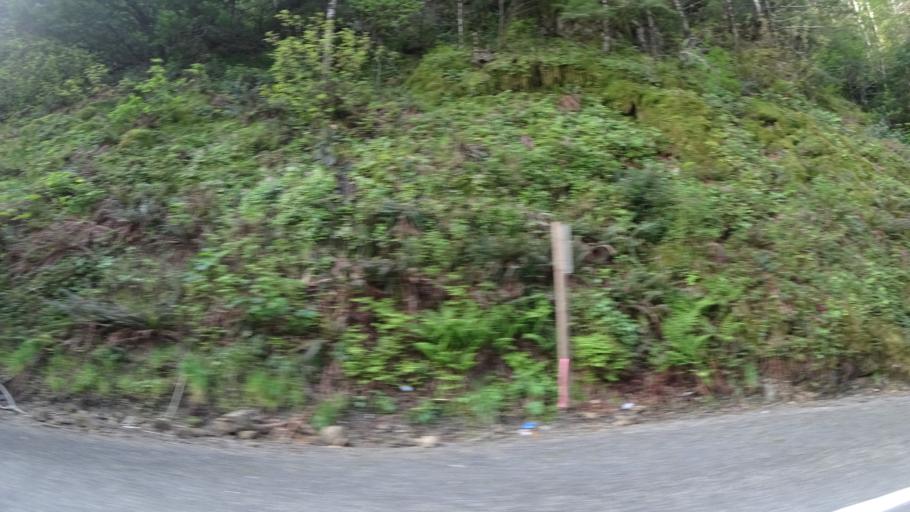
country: US
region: Oregon
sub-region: Curry County
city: Port Orford
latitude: 42.6844
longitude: -124.4259
